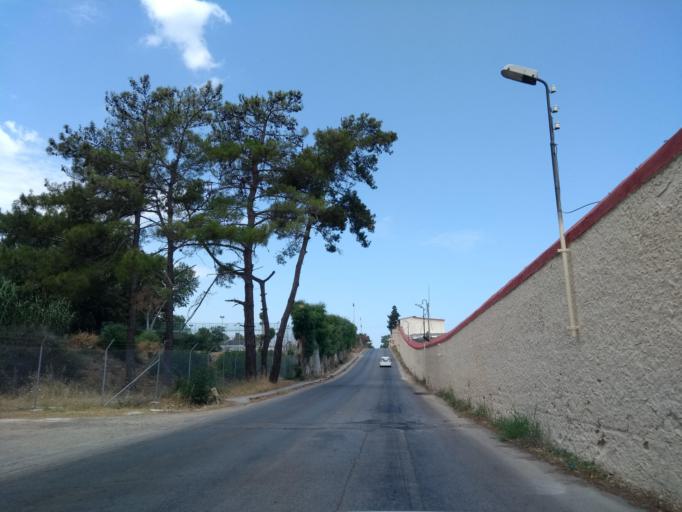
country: GR
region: Crete
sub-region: Nomos Chanias
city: Souda
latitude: 35.4859
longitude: 24.0836
